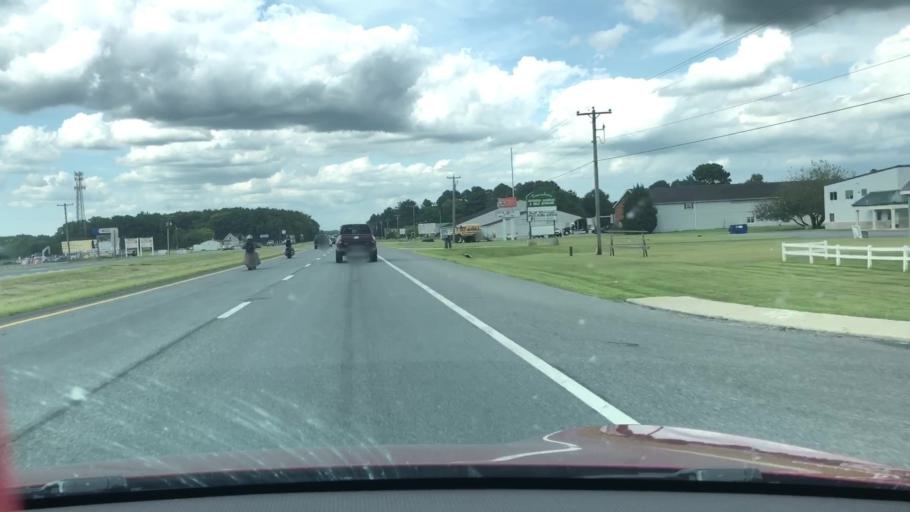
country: US
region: Delaware
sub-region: Sussex County
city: Delmar
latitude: 38.4642
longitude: -75.5579
